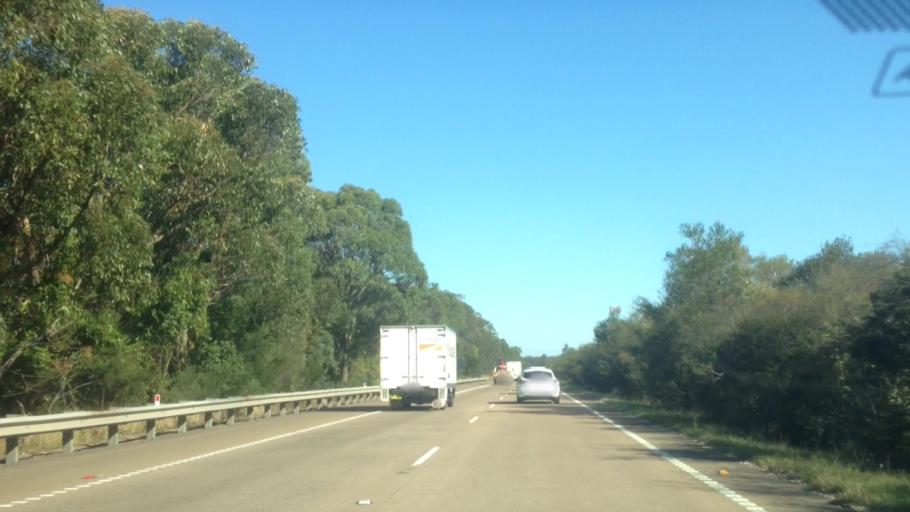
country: AU
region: New South Wales
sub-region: Wyong Shire
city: Charmhaven
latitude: -33.1587
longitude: 151.4703
